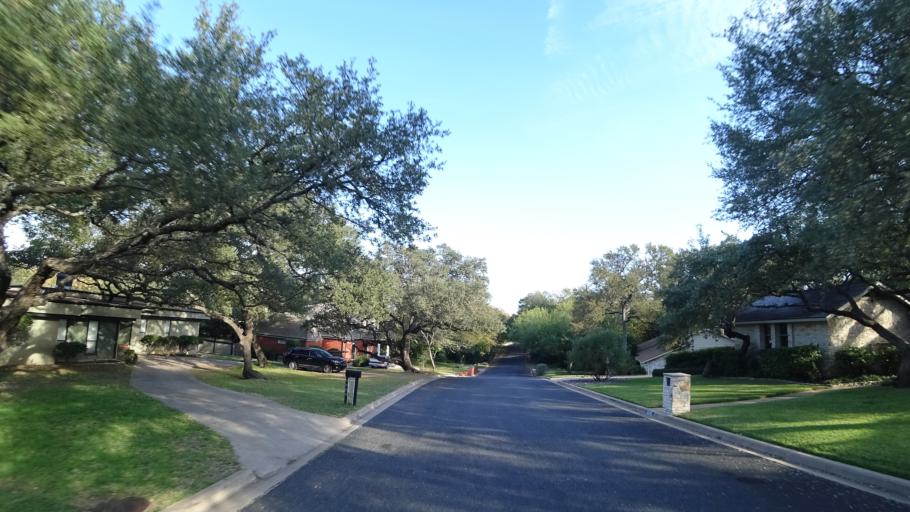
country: US
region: Texas
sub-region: Williamson County
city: Anderson Mill
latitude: 30.4394
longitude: -97.8031
